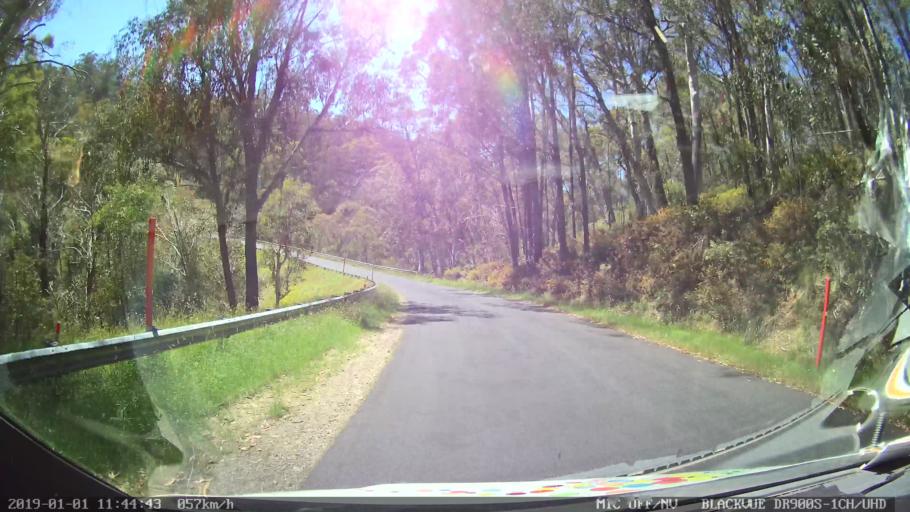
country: AU
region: New South Wales
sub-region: Snowy River
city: Jindabyne
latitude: -35.9009
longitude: 148.3949
